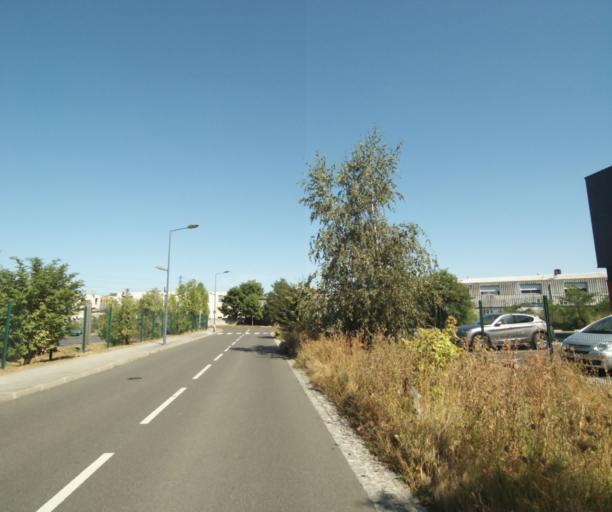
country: FR
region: Ile-de-France
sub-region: Departement des Hauts-de-Seine
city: Villeneuve-la-Garenne
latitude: 48.9274
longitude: 2.3223
